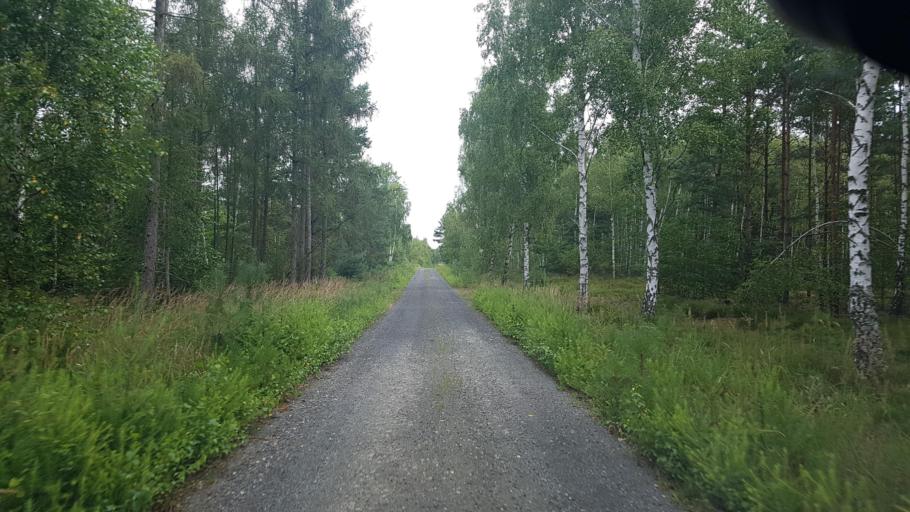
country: DE
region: Brandenburg
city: Grossraschen
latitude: 51.6213
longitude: 13.9688
